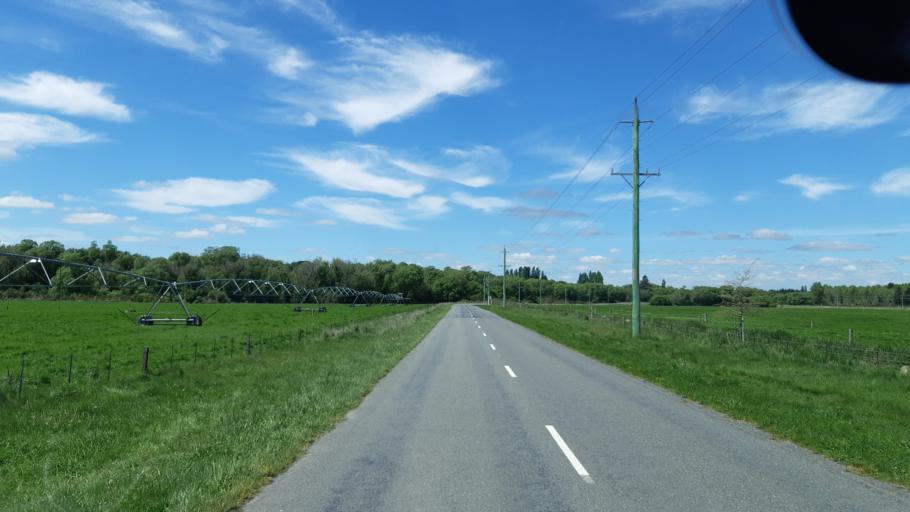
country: NZ
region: Canterbury
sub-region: Ashburton District
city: Methven
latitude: -43.7325
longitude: 171.5253
